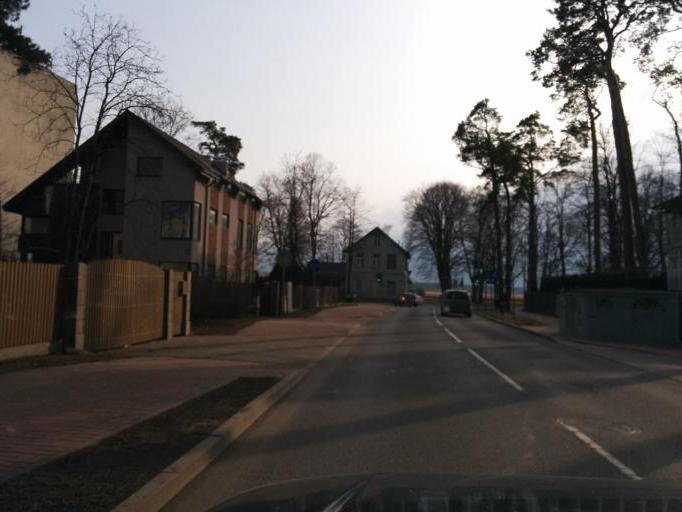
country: LV
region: Jurmala
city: Jurmala
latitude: 56.9731
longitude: 23.7913
